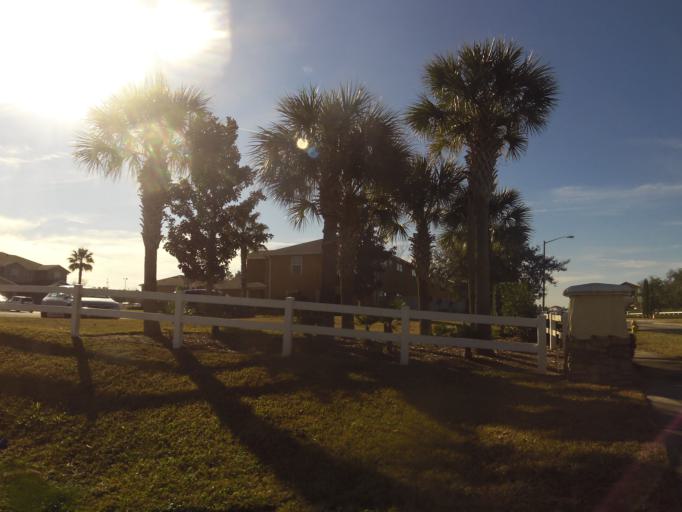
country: US
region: Florida
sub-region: Saint Johns County
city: Saint Augustine
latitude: 29.9246
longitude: -81.4035
